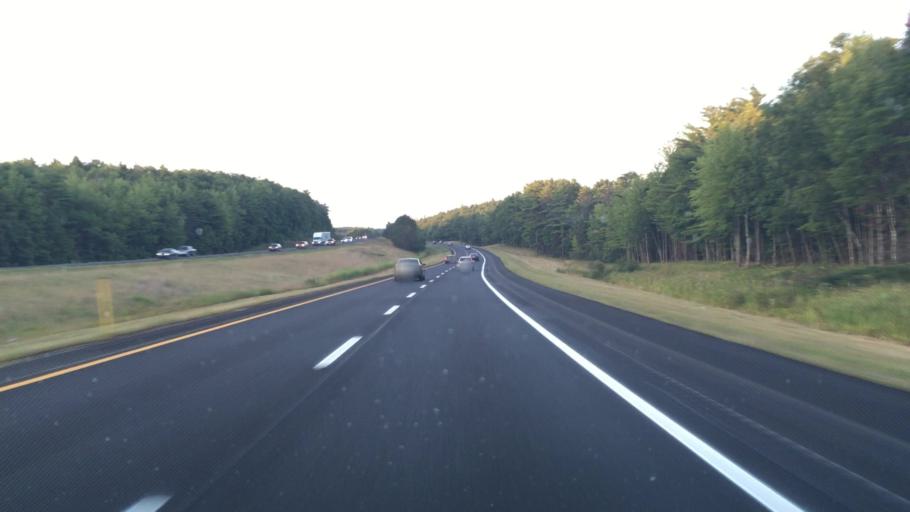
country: US
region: Maine
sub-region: Sagadahoc County
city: Topsham
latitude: 43.9823
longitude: -69.9434
